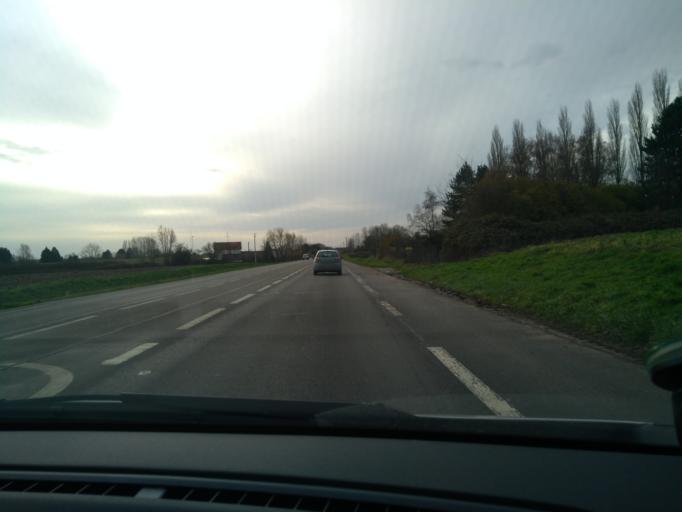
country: FR
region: Nord-Pas-de-Calais
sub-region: Departement du Nord
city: Maubeuge
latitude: 50.3201
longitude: 3.9762
